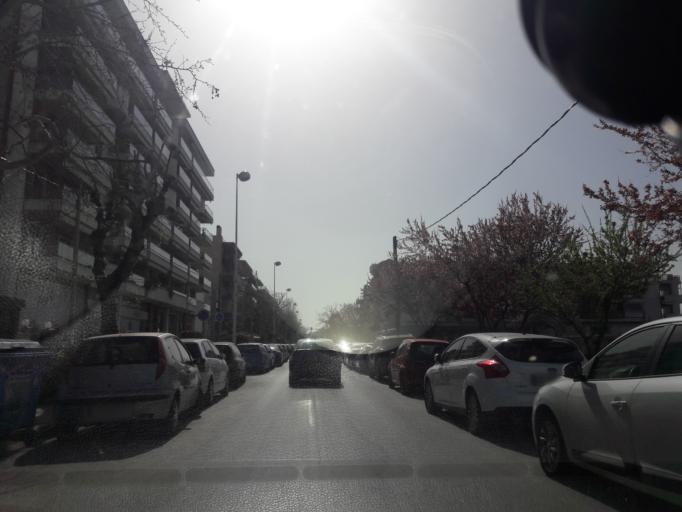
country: GR
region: Central Macedonia
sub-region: Nomos Thessalonikis
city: Kalamaria
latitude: 40.5904
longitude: 22.9466
